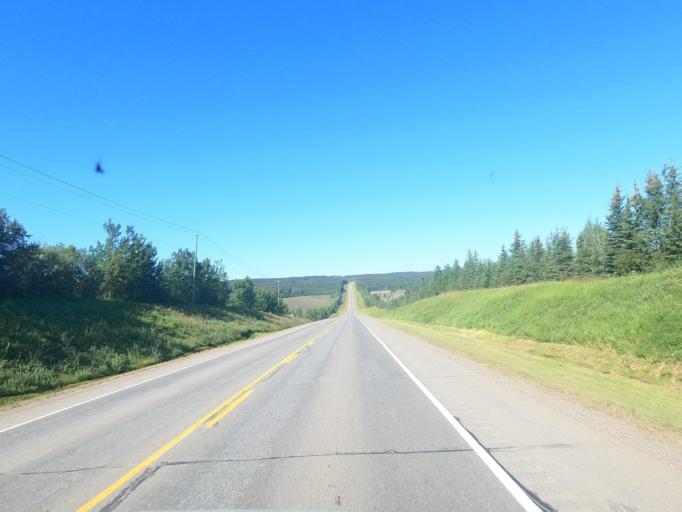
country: CA
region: British Columbia
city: Fort St. John
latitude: 56.6298
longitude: -121.5291
